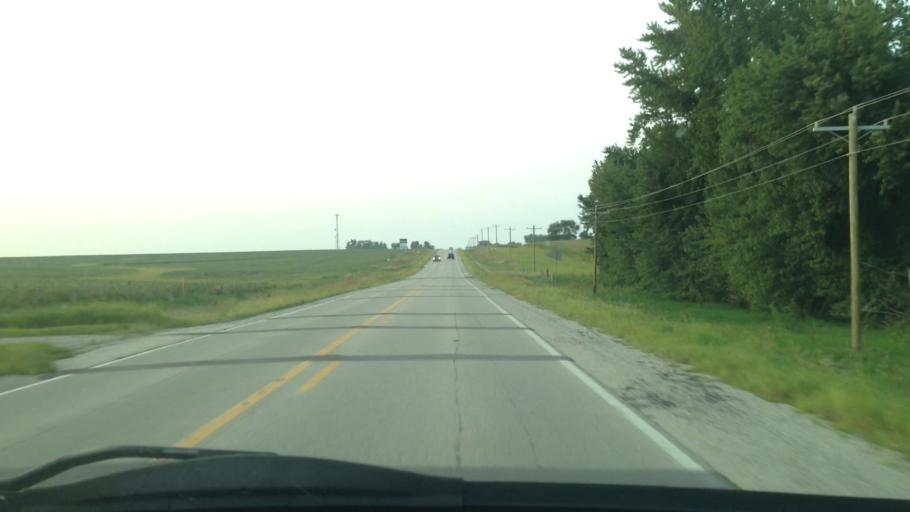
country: US
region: Iowa
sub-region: Benton County
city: Atkins
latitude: 42.0691
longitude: -91.8691
